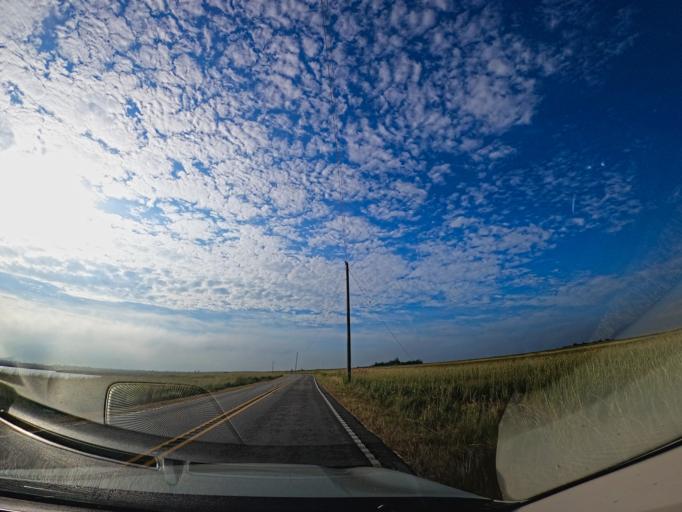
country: US
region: Louisiana
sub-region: Terrebonne Parish
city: Dulac
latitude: 29.3034
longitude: -90.6635
